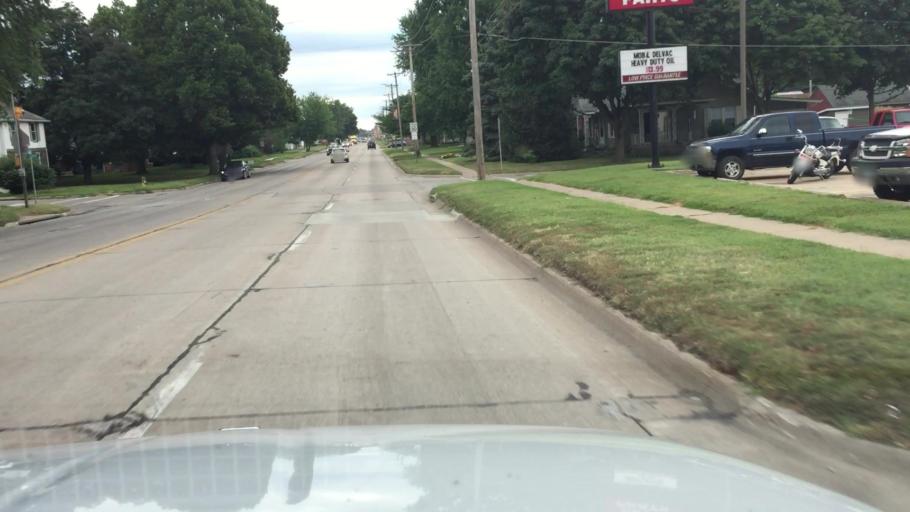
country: US
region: Iowa
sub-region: Lee County
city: Fort Madison
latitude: 40.6267
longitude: -91.3534
